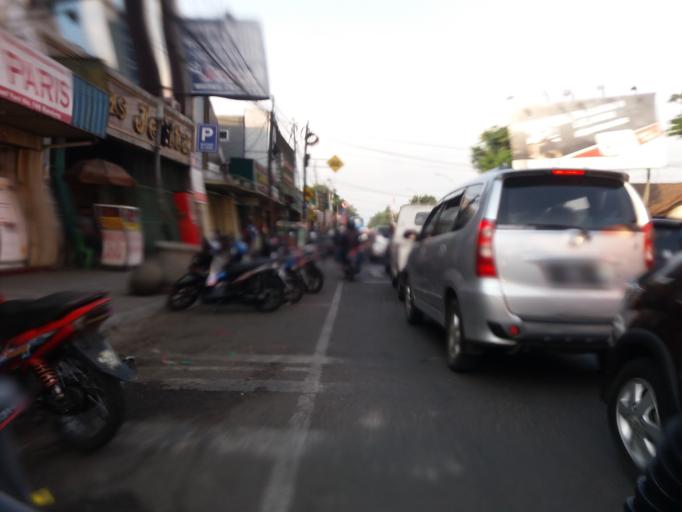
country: ID
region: West Java
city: Bandung
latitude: -6.9190
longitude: 107.6238
